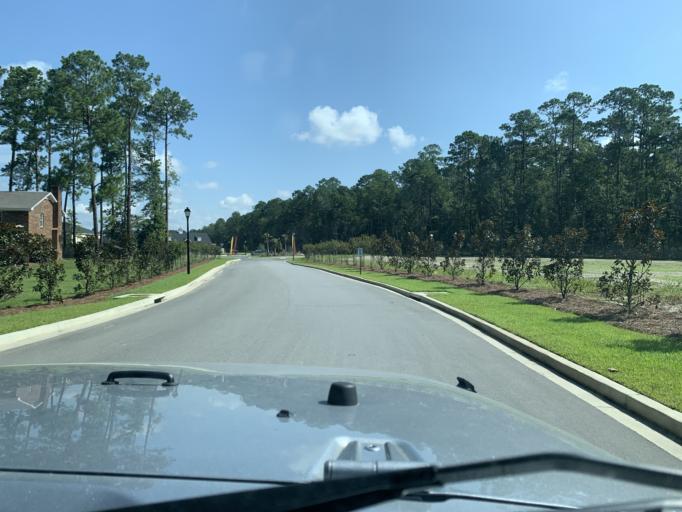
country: US
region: Georgia
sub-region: Chatham County
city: Bloomingdale
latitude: 32.1303
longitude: -81.2911
